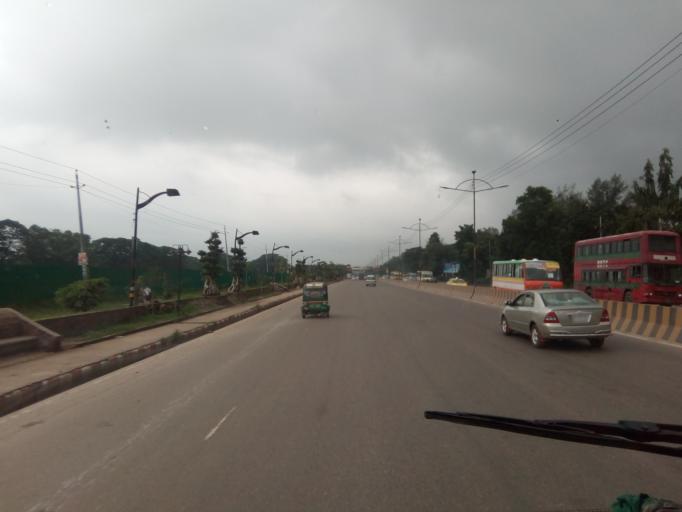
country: BD
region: Dhaka
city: Tungi
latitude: 23.8489
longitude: 90.4099
